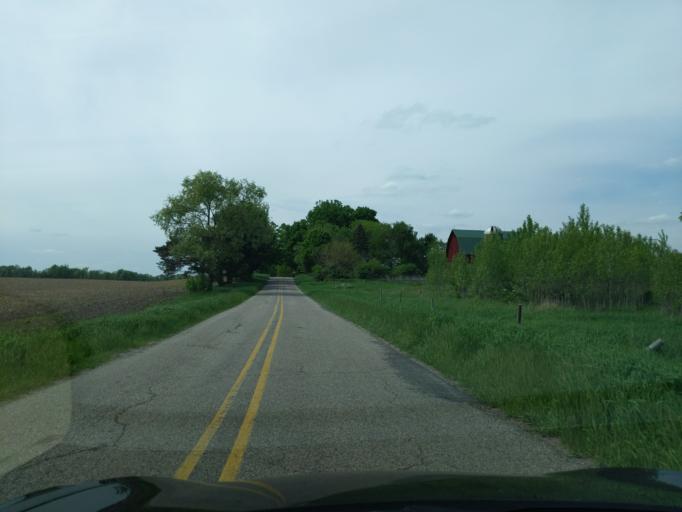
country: US
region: Michigan
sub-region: Ingham County
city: Leslie
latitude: 42.4287
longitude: -84.3356
